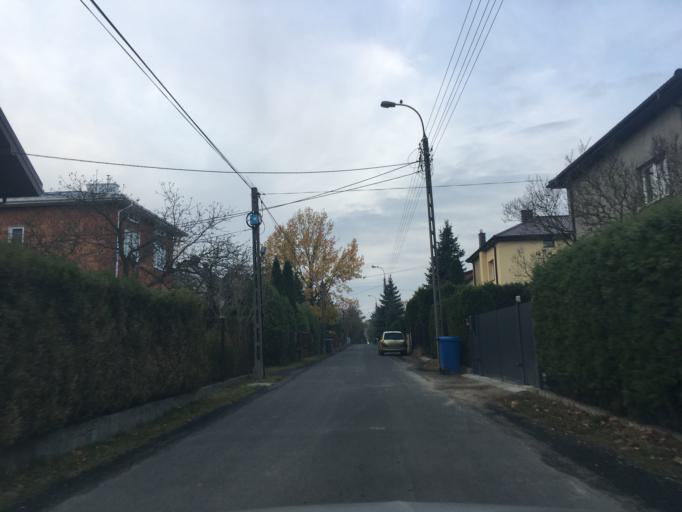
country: PL
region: Masovian Voivodeship
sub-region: Powiat pruszkowski
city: Brwinow
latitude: 52.1415
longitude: 20.7313
